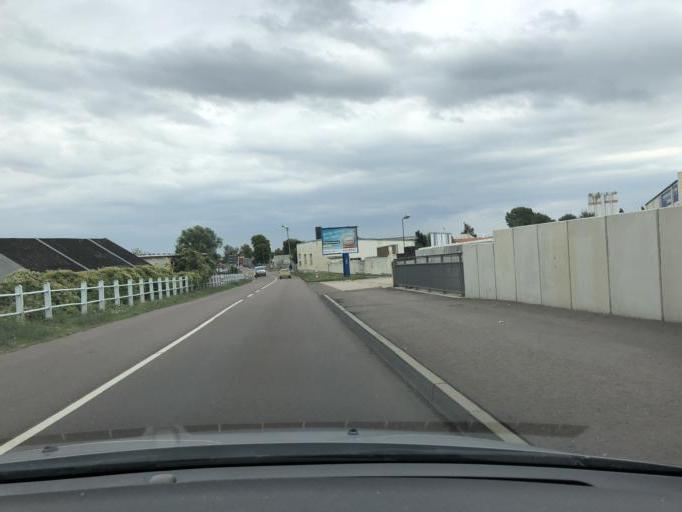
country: DE
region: Saxony-Anhalt
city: Koethen
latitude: 51.7440
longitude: 11.9939
